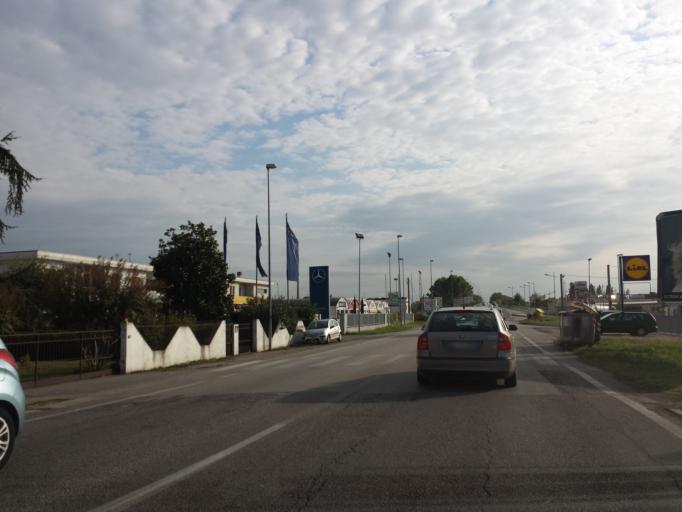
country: IT
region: Veneto
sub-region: Provincia di Rovigo
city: Rovigo
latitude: 45.0586
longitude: 11.7914
